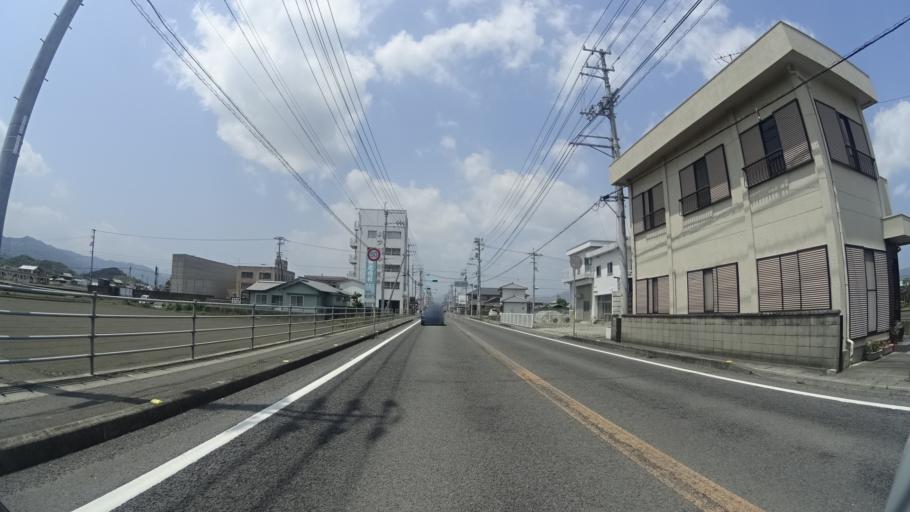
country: JP
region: Tokushima
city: Ishii
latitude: 34.0712
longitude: 134.4010
